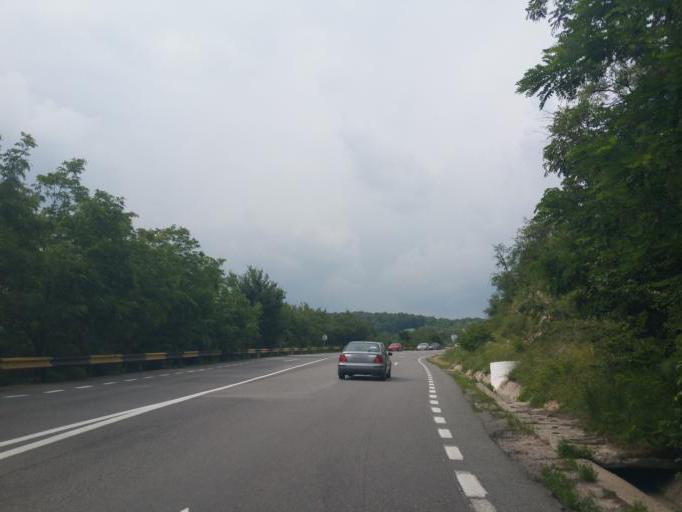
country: RO
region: Salaj
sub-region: Comuna Treznea
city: Treznea
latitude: 47.1266
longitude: 23.1293
